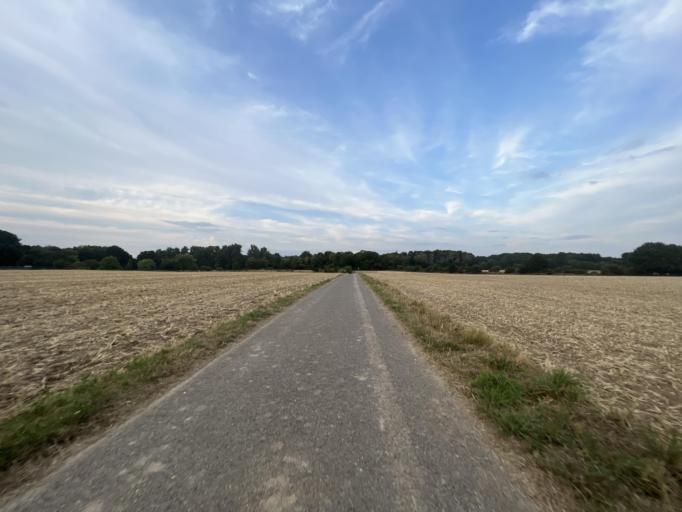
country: DE
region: North Rhine-Westphalia
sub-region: Regierungsbezirk Koln
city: Dueren
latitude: 50.8086
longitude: 6.4495
